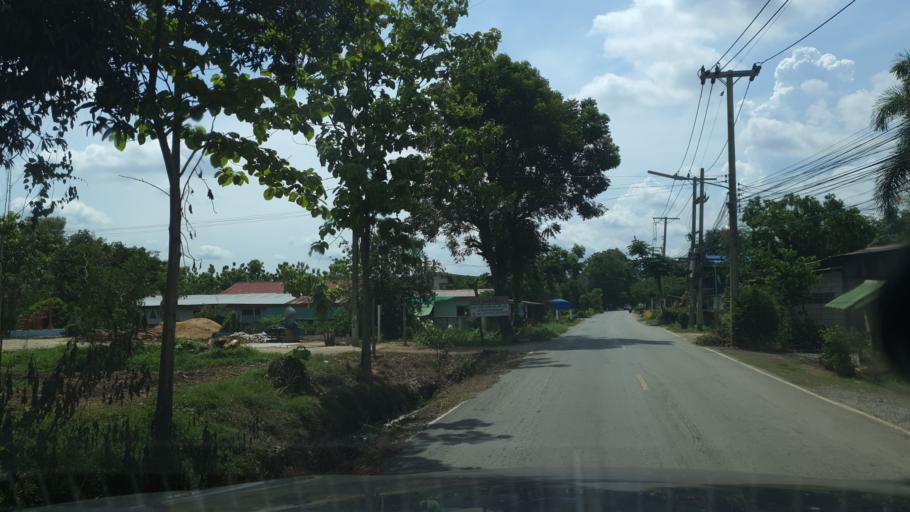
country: TH
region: Sukhothai
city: Sukhothai
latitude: 16.9959
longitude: 99.8459
